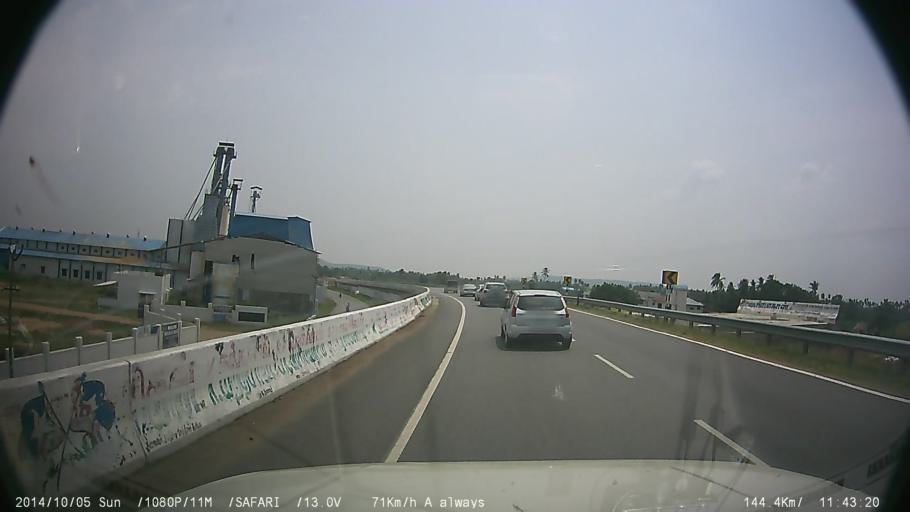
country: IN
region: Tamil Nadu
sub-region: Salem
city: Attur
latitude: 11.5934
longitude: 78.6204
